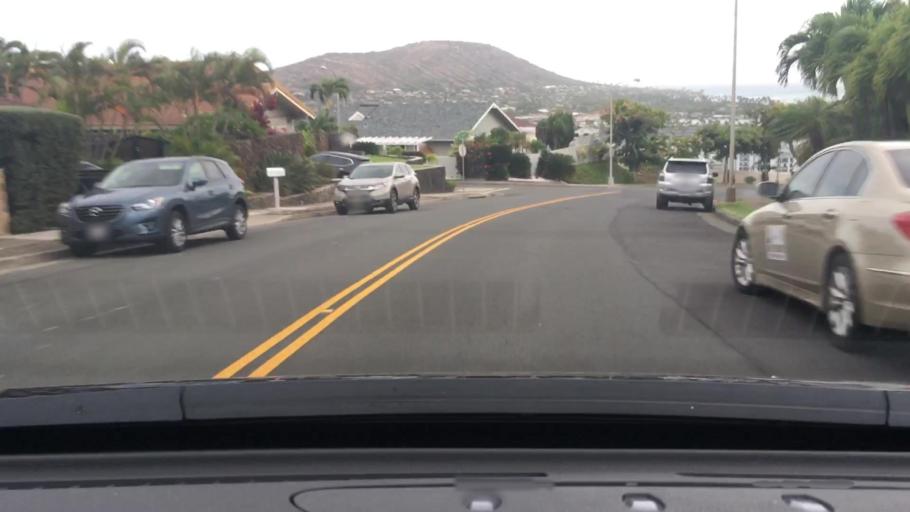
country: US
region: Hawaii
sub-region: Honolulu County
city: Waimanalo Beach
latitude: 21.2921
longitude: -157.7027
